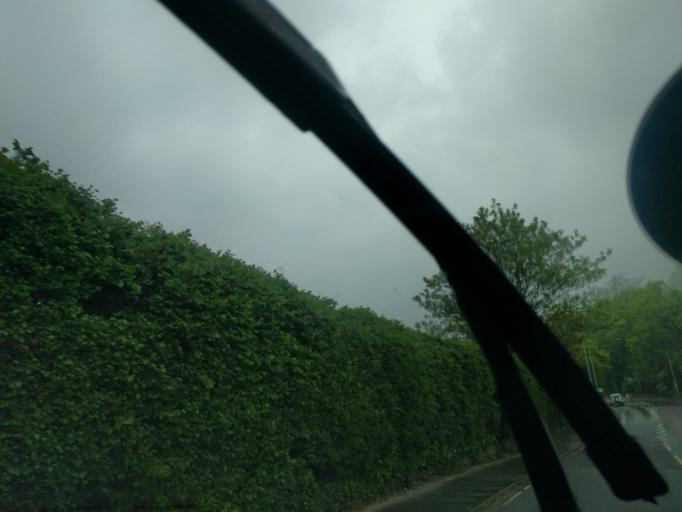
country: GB
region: England
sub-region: Wiltshire
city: Chippenham
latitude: 51.4713
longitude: -2.1248
